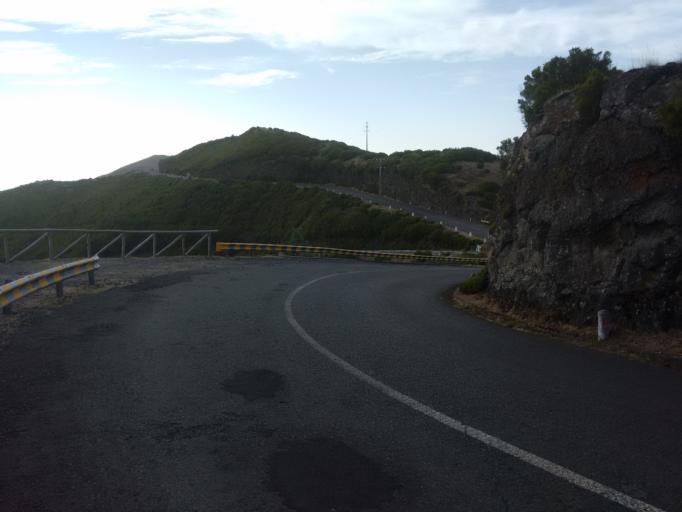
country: PT
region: Madeira
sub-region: Calheta
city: Arco da Calheta
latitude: 32.7580
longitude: -17.1385
